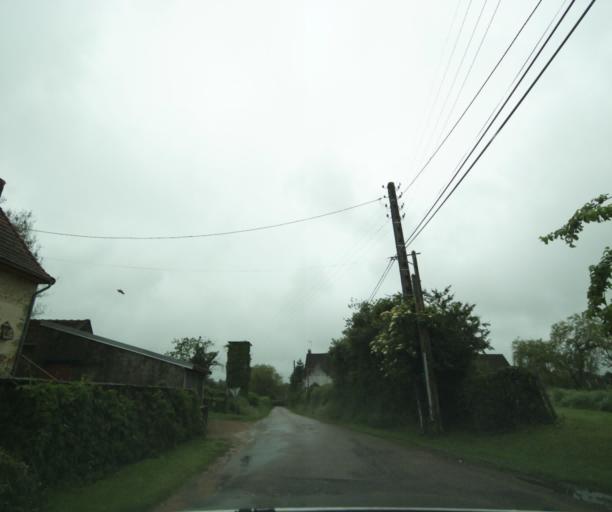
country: FR
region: Bourgogne
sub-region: Departement de Saone-et-Loire
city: Charolles
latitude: 46.4417
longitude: 4.3181
